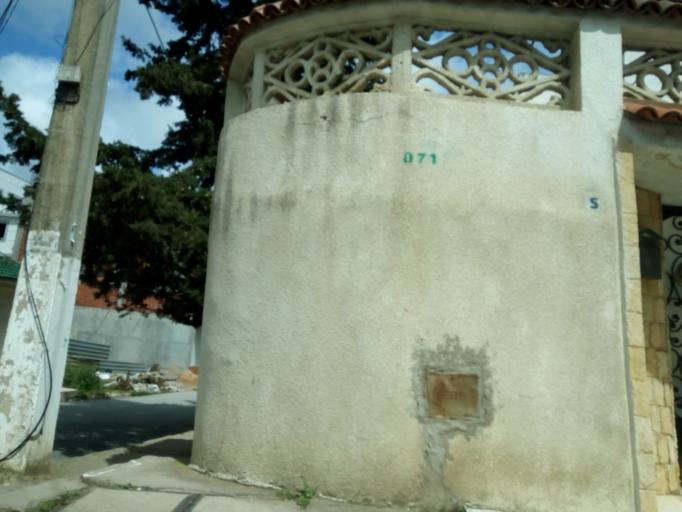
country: DZ
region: Tipaza
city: Douera
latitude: 36.7017
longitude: 2.9703
